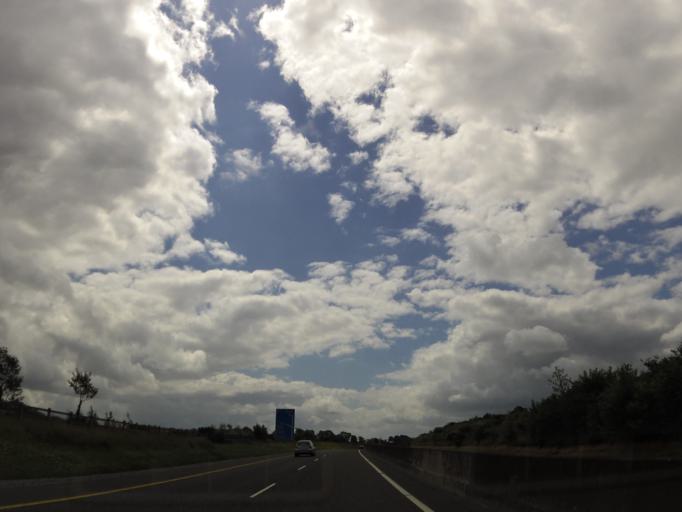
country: IE
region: Munster
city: Cashel
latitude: 52.5227
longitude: -7.8589
